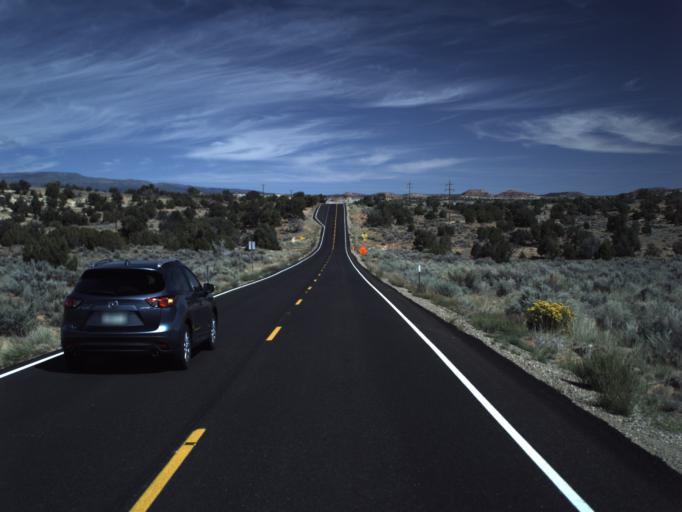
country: US
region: Utah
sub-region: Wayne County
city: Loa
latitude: 37.7622
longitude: -111.4306
